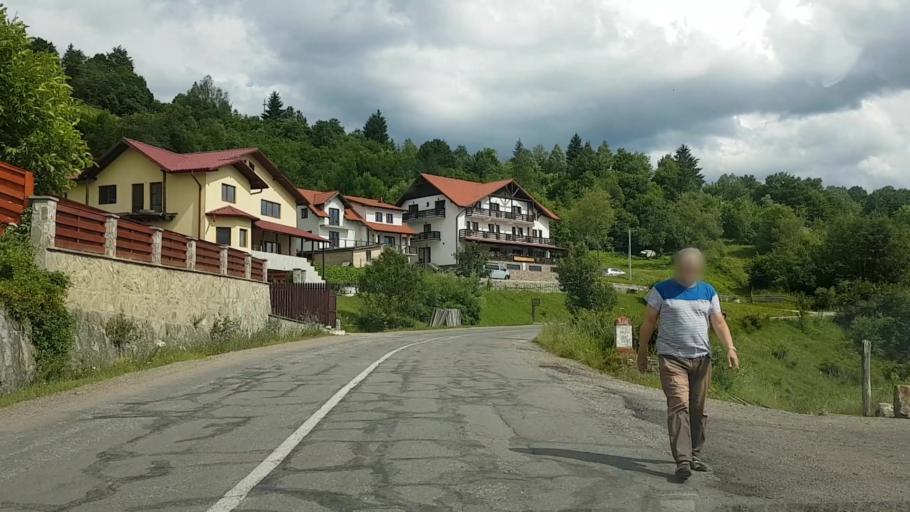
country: RO
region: Neamt
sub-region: Comuna Bicaz
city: Dodeni
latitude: 46.9923
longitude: 26.1012
